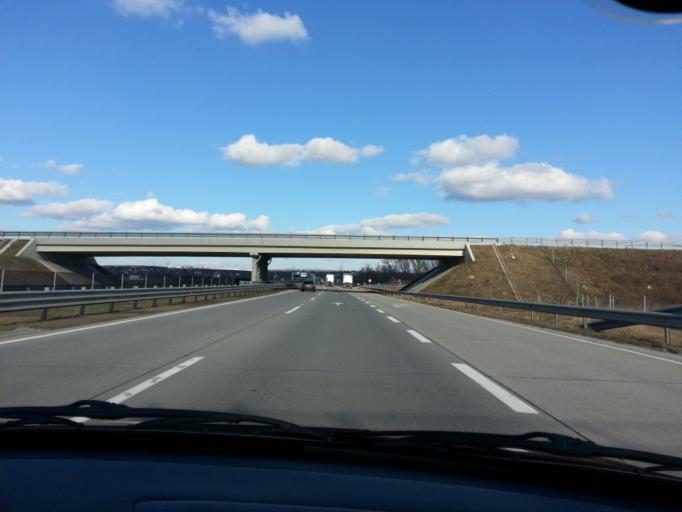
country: HU
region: Pest
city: Ecser
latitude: 47.4302
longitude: 19.3261
